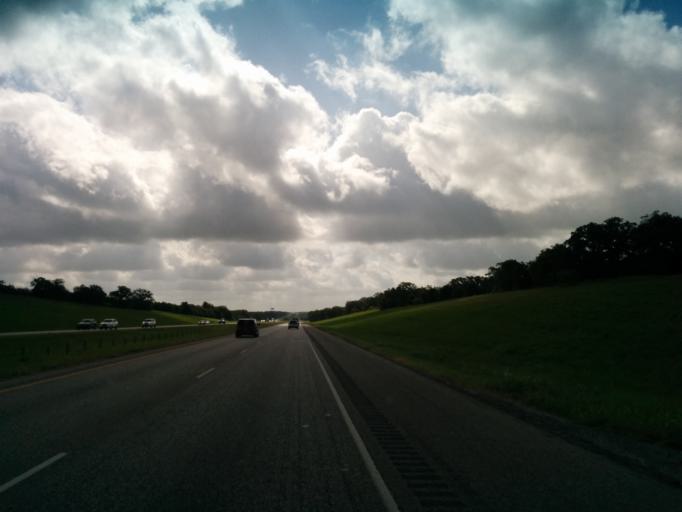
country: US
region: Texas
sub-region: Caldwell County
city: Luling
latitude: 29.6526
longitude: -97.5452
